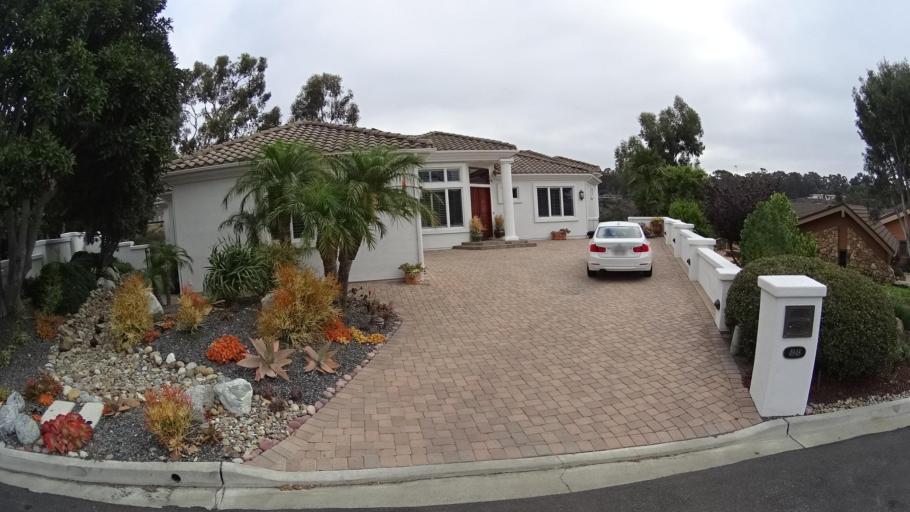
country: US
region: California
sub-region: San Diego County
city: Fairbanks Ranch
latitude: 32.9873
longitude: -117.2276
